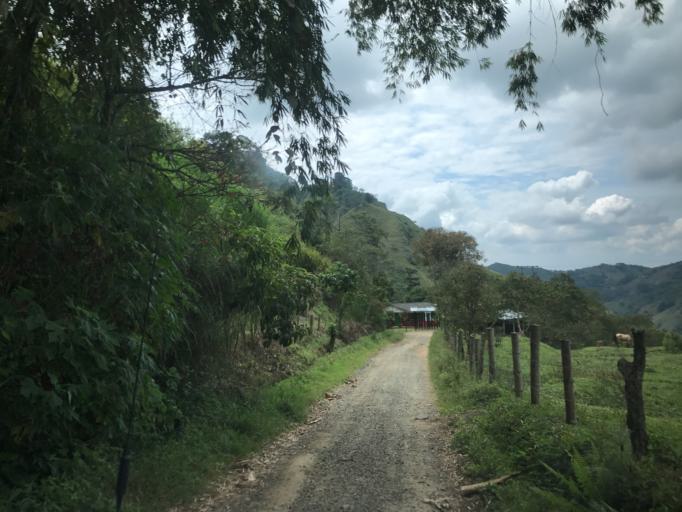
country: CO
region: Valle del Cauca
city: Obando
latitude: 4.5581
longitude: -75.8991
